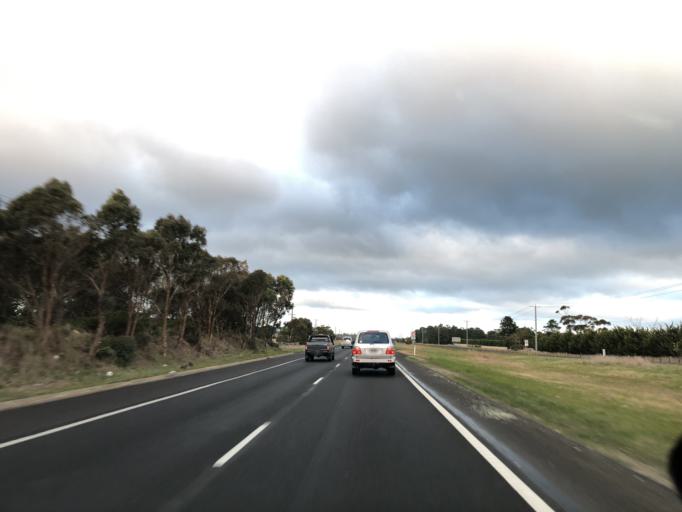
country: AU
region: Victoria
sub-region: Hume
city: Sunbury
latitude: -37.5472
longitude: 144.6521
